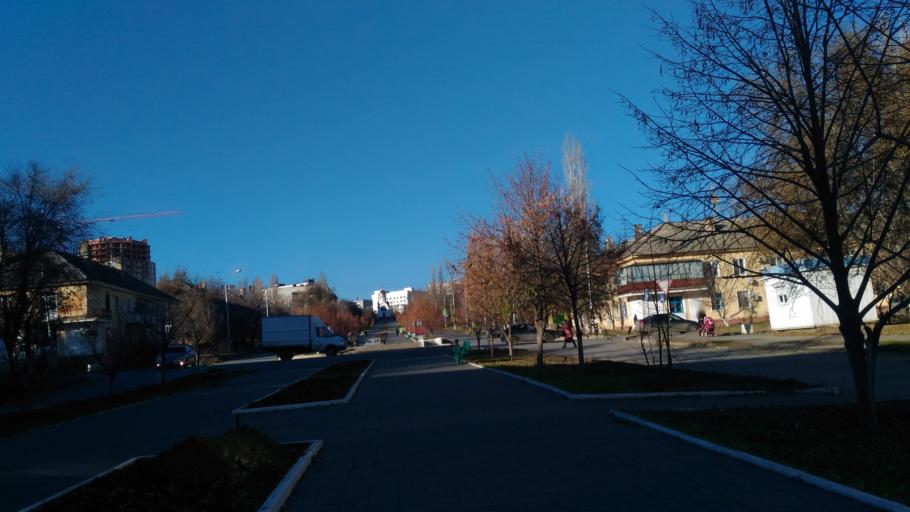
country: RU
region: Volgograd
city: Volgograd
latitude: 48.6606
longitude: 44.4453
